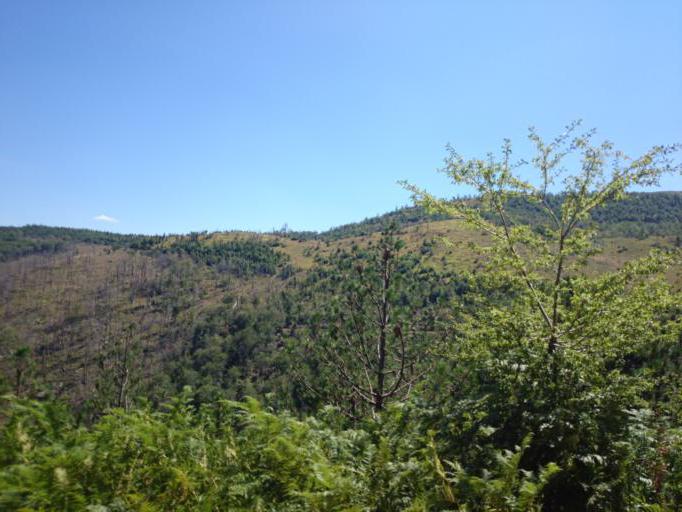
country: AL
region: Diber
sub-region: Rrethi i Bulqizes
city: Zerqan
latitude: 41.4244
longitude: 20.3210
